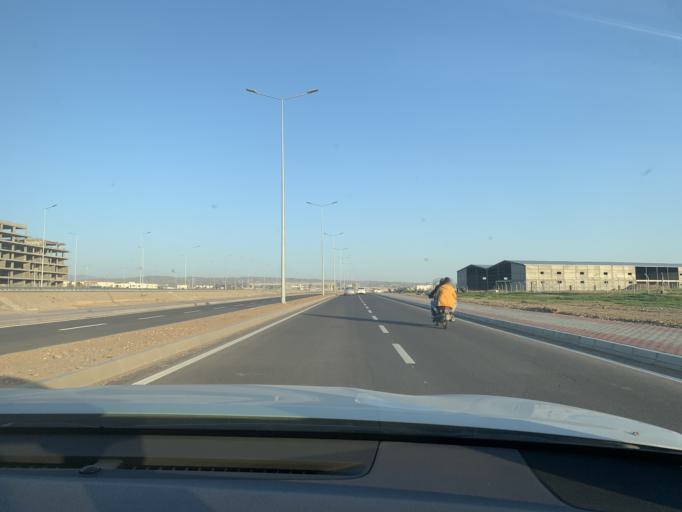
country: IQ
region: Arbil
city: Erbil
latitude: 36.2844
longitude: 44.0509
